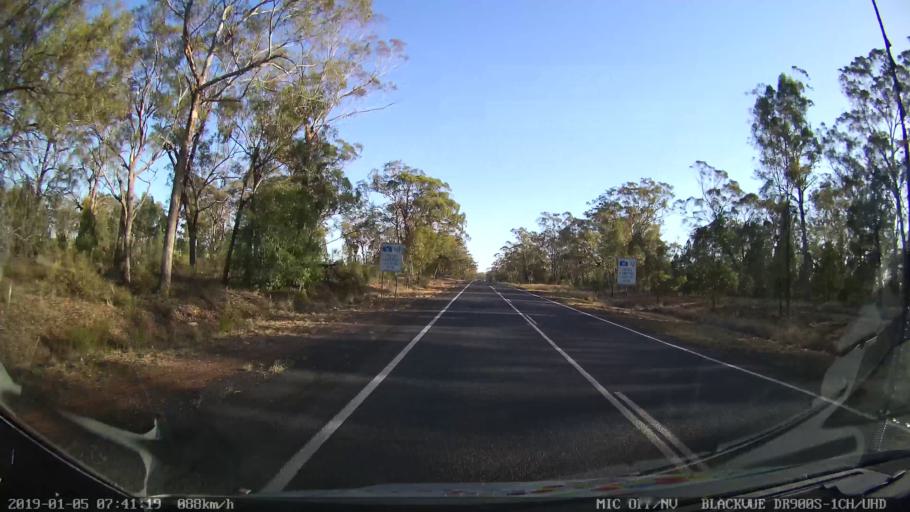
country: AU
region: New South Wales
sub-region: Gilgandra
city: Gilgandra
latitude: -31.9123
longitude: 148.6204
